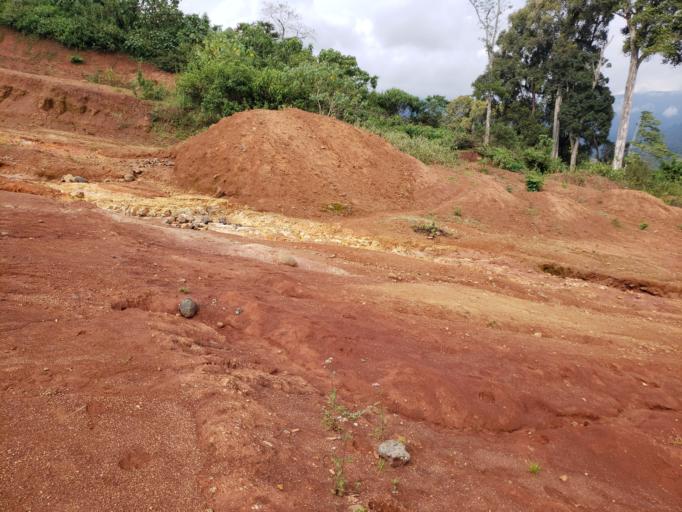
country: ET
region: Oromiya
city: Dodola
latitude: 6.5441
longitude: 39.4224
